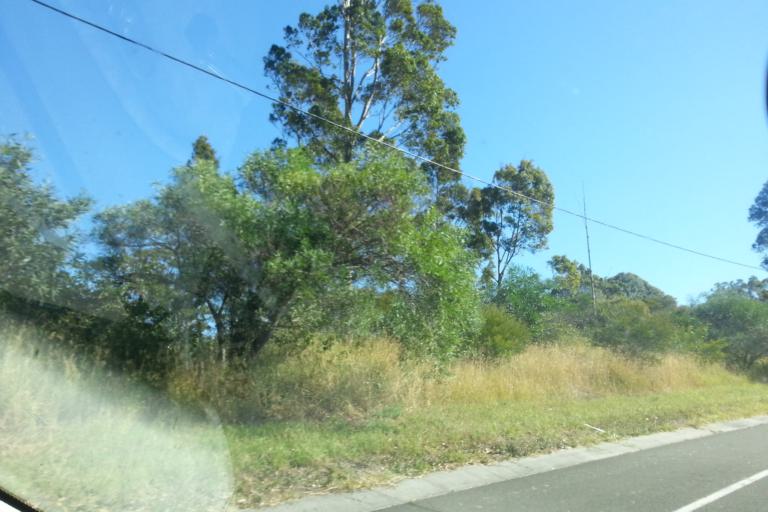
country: AU
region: New South Wales
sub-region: Wollongong
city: Dapto
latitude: -34.5191
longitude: 150.7841
